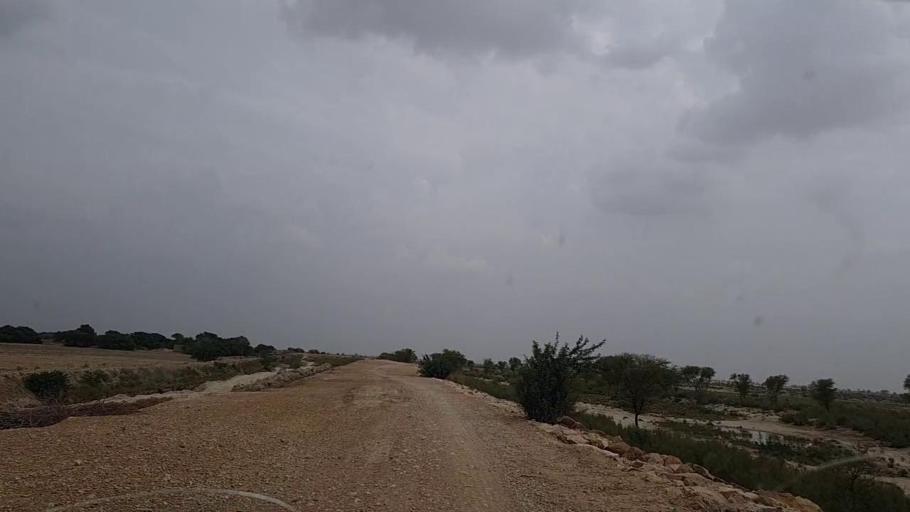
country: PK
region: Sindh
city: Johi
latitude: 26.7245
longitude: 67.5781
